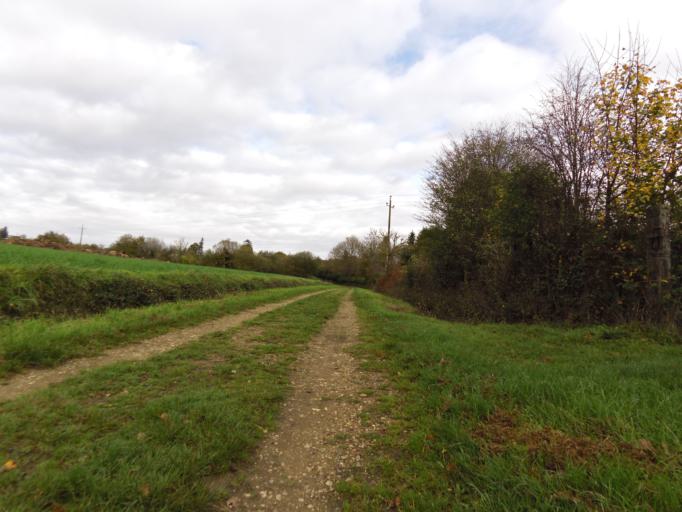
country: FR
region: Brittany
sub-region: Departement d'Ille-et-Vilaine
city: Crevin
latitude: 47.9573
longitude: -1.6516
